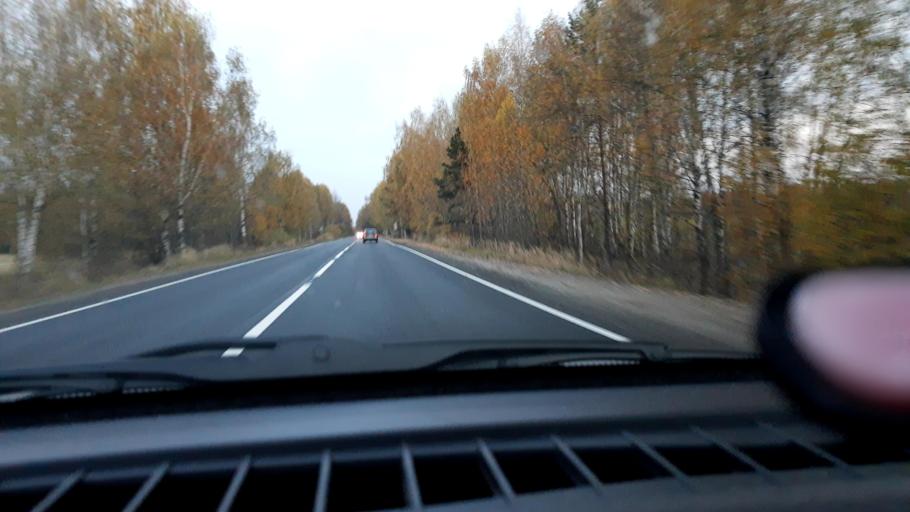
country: RU
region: Nizjnij Novgorod
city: Novaya Balakhna
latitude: 56.5535
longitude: 43.7440
